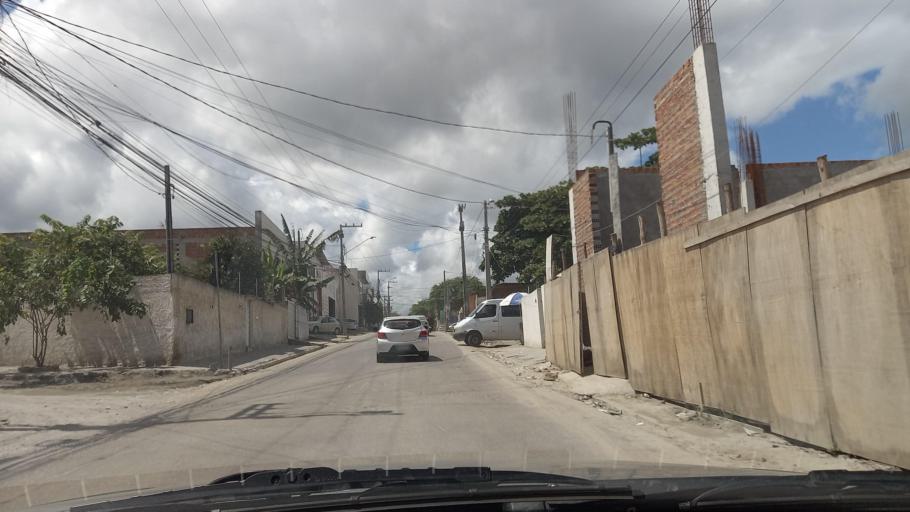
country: BR
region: Pernambuco
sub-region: Caruaru
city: Caruaru
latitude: -8.2823
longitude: -35.9537
